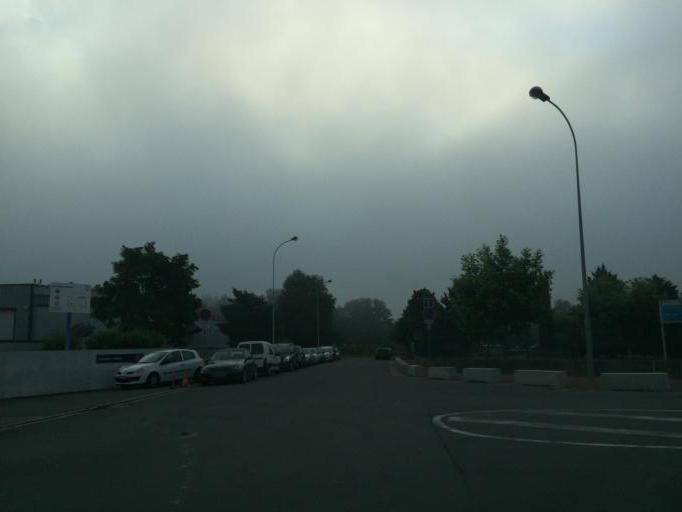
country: FR
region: Rhone-Alpes
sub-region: Departement de l'Ain
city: Jassans-Riottier
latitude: 45.9895
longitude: 4.7452
